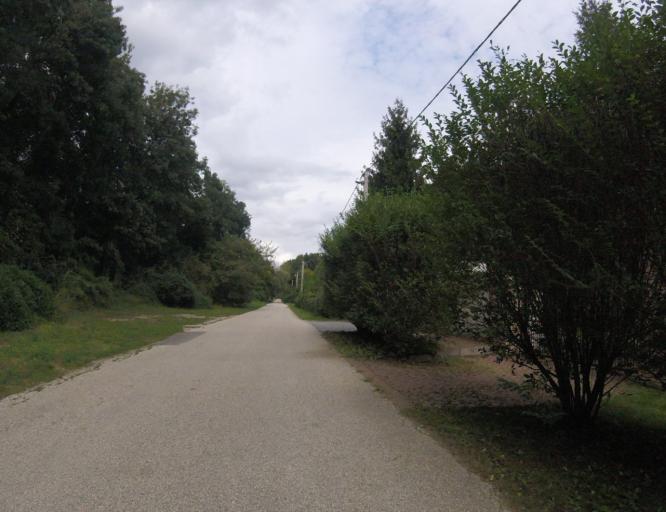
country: HU
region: Pest
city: Szigetcsep
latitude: 47.2853
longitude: 19.0012
